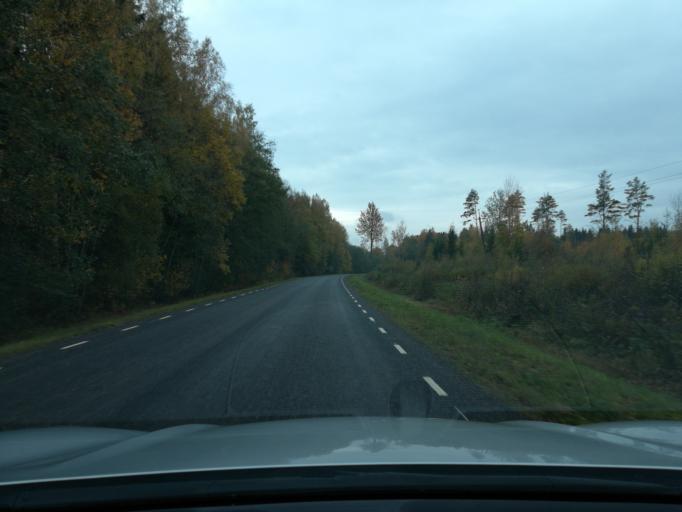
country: EE
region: Ida-Virumaa
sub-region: Johvi vald
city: Johvi
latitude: 59.0454
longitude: 27.3961
